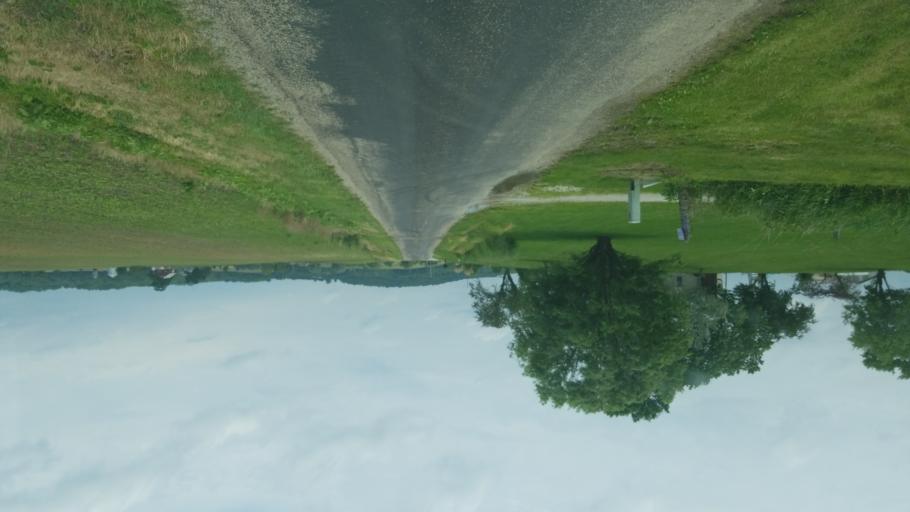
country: US
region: Ohio
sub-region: Perry County
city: Thornport
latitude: 39.9153
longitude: -82.3702
